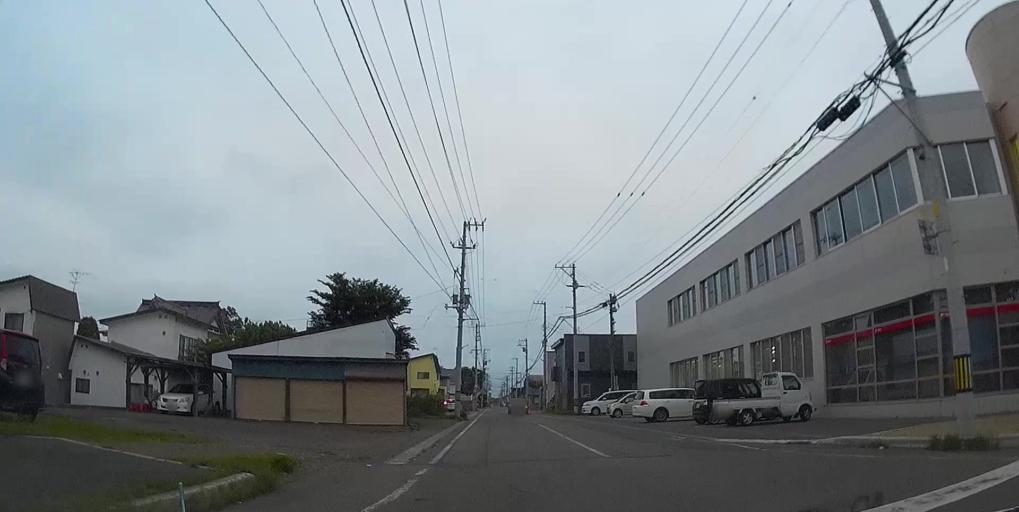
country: JP
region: Hokkaido
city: Nanae
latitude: 42.2573
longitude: 140.2685
